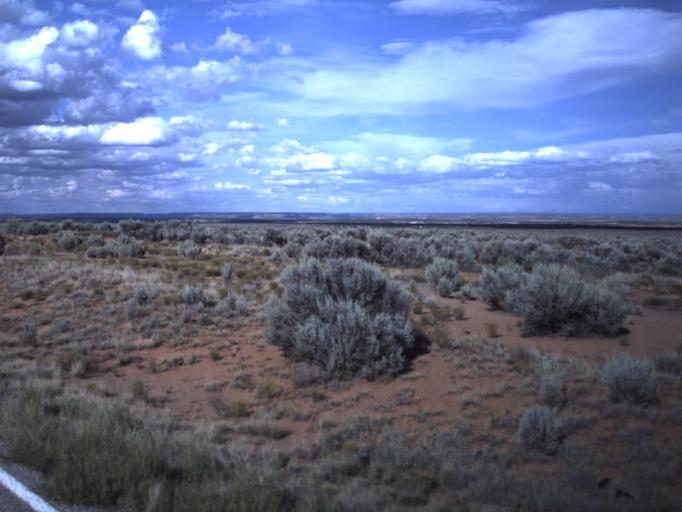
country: US
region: Utah
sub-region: San Juan County
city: Blanding
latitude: 37.3825
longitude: -109.3410
